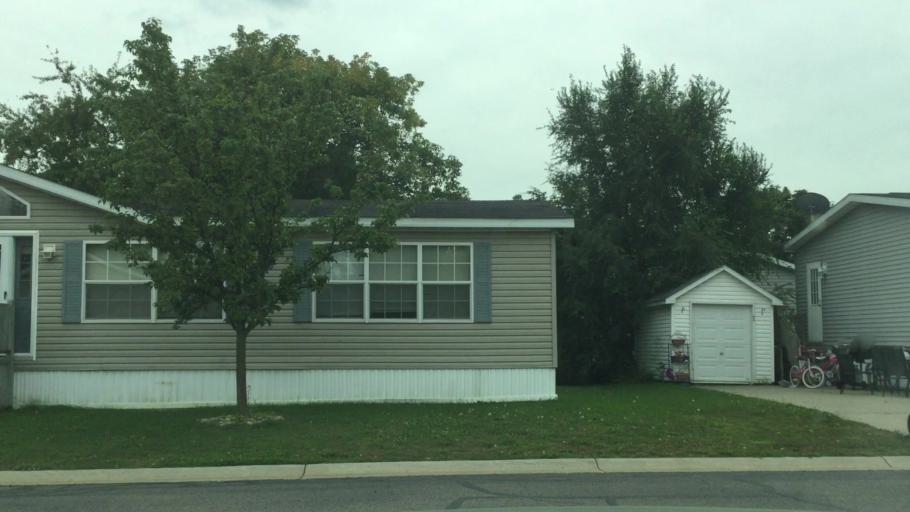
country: US
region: Michigan
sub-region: Oakland County
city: Waterford
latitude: 42.6609
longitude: -83.4717
